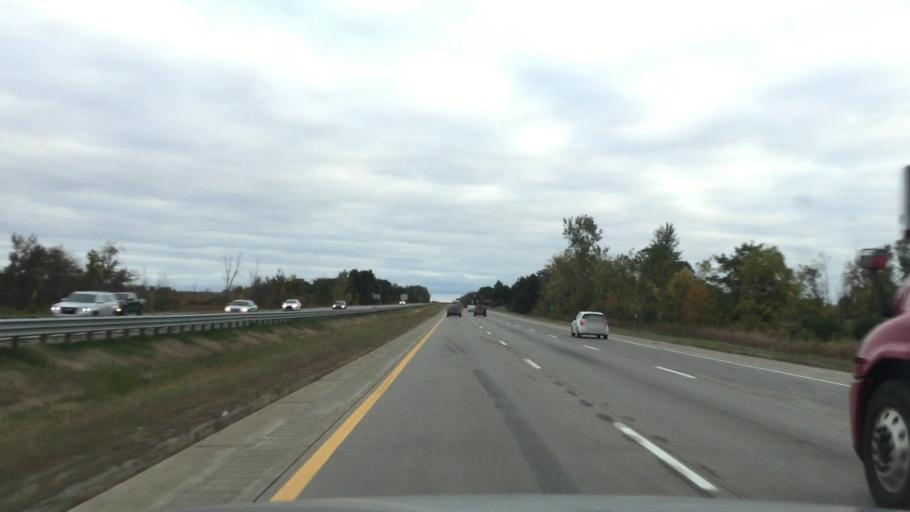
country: US
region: Michigan
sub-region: Genesee County
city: Lake Fenton
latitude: 42.8652
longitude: -83.7396
